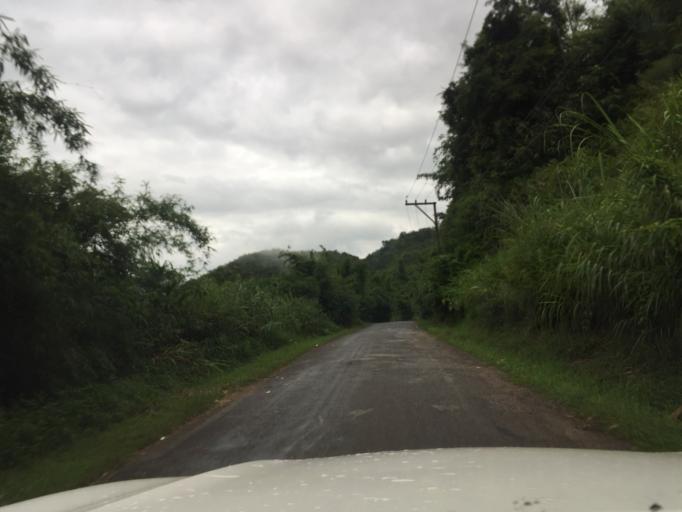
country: LA
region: Oudomxai
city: Muang La
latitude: 20.9459
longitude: 102.2092
